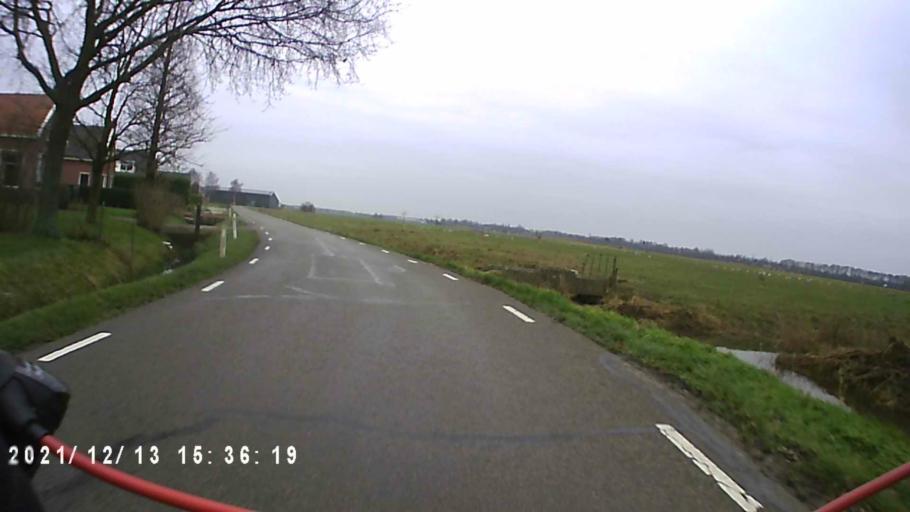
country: NL
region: Groningen
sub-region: Gemeente Appingedam
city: Appingedam
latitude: 53.3297
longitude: 6.8293
